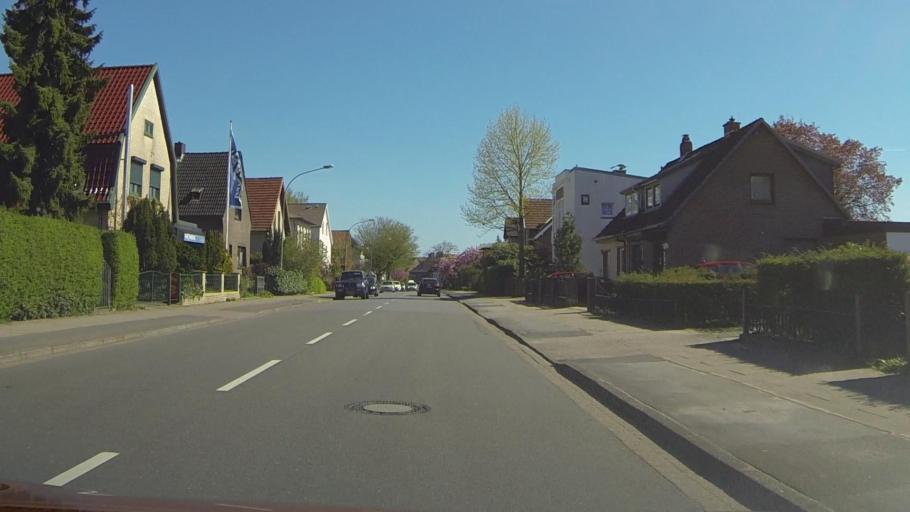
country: DE
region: Schleswig-Holstein
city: Pinneberg
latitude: 53.6670
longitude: 9.7872
